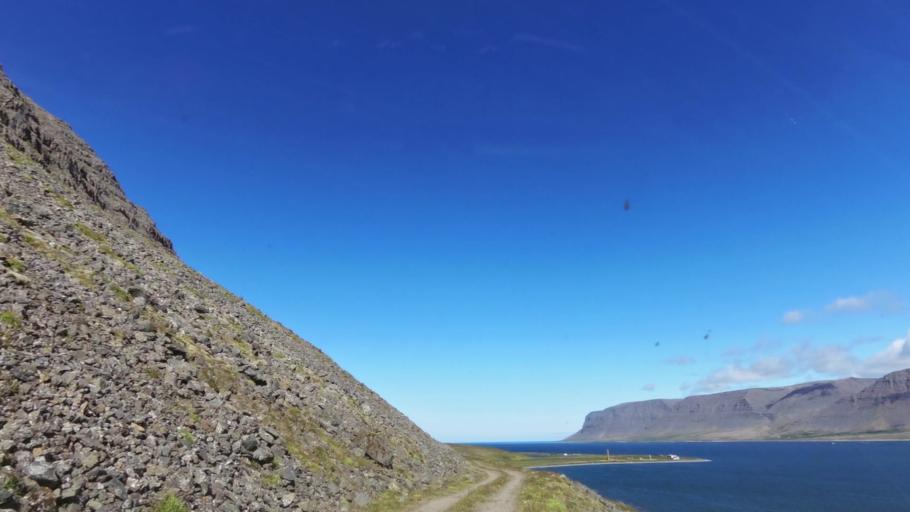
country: IS
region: West
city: Olafsvik
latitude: 65.6330
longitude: -23.9205
